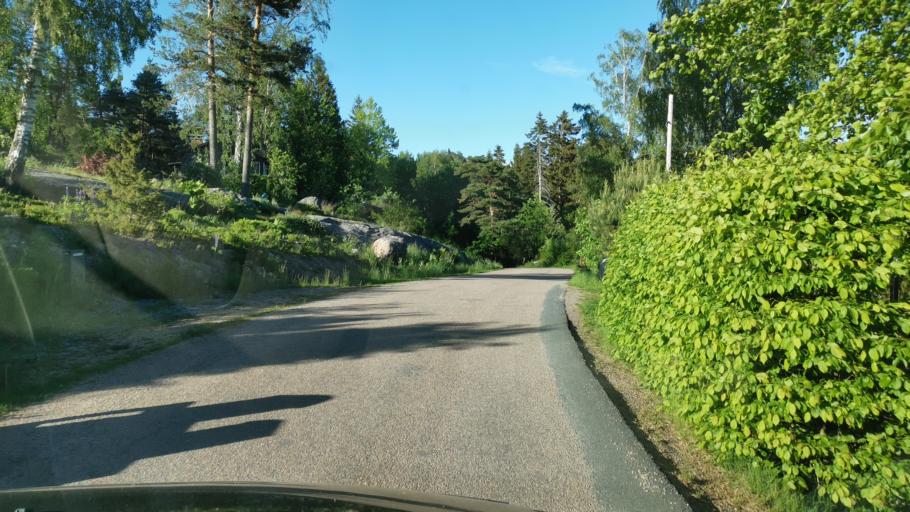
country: SE
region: Vaestra Goetaland
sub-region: Orust
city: Henan
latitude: 58.2686
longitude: 11.6360
